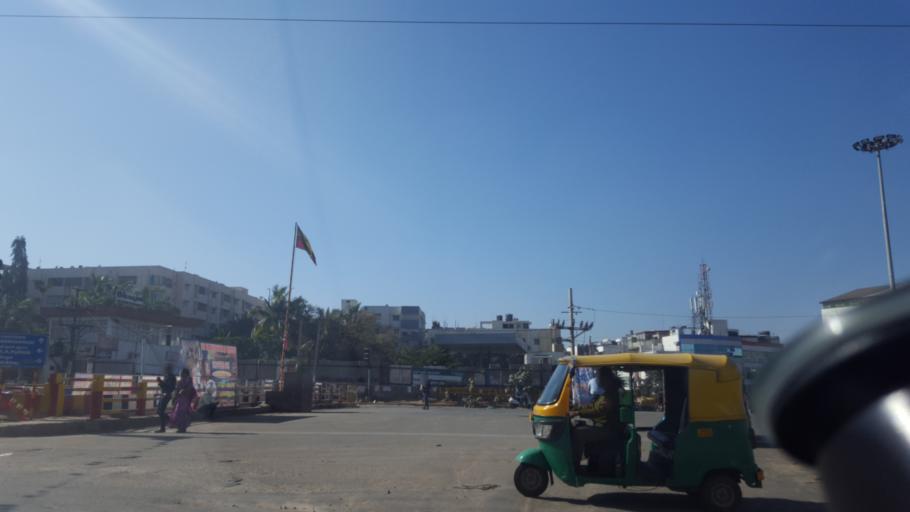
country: IN
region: Karnataka
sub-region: Bangalore Urban
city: Bangalore
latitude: 13.0194
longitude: 77.6559
